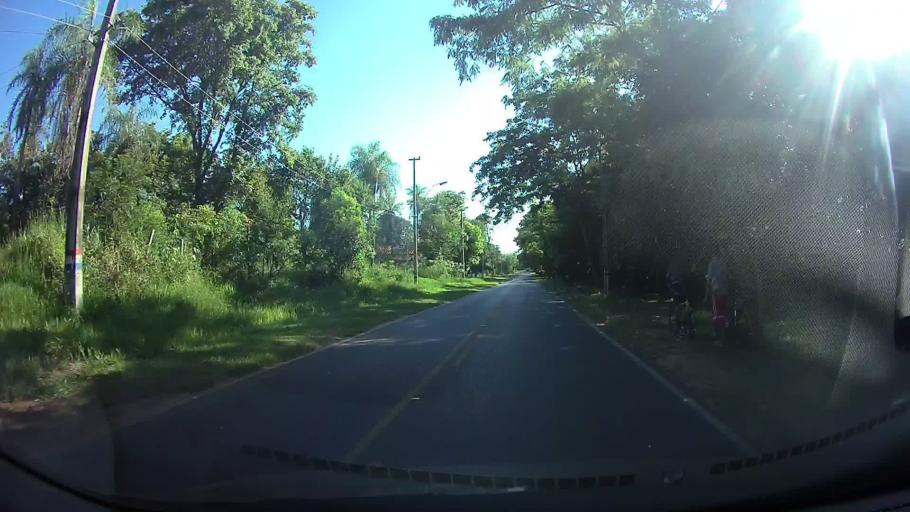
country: PY
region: Cordillera
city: Atyra
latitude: -25.2919
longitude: -57.1821
